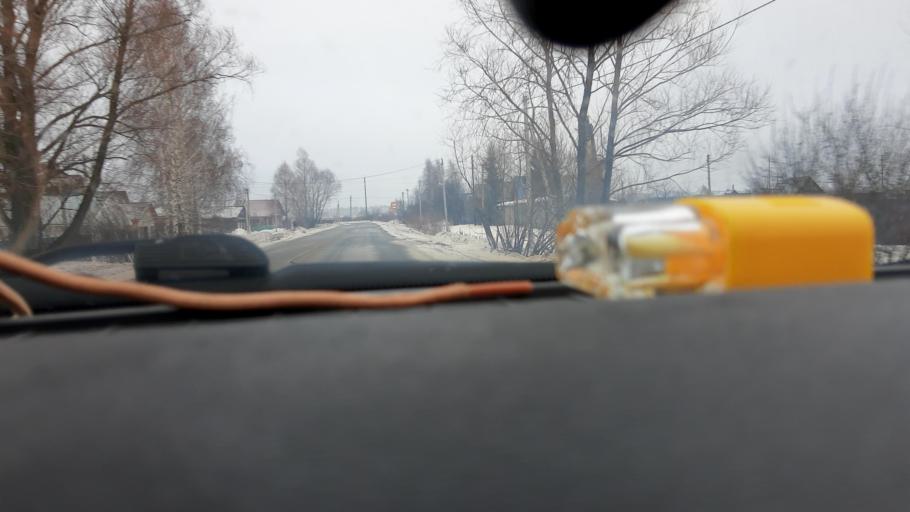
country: RU
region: Bashkortostan
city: Iglino
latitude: 54.7354
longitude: 56.3964
